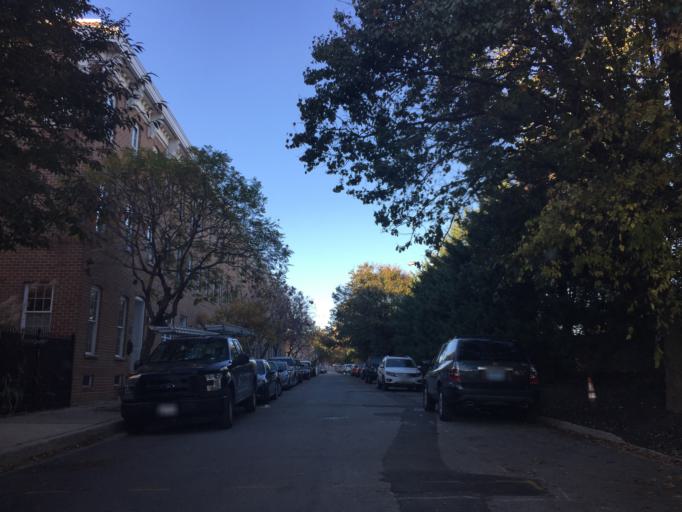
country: US
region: Maryland
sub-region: City of Baltimore
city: Baltimore
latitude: 39.2689
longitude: -76.6041
